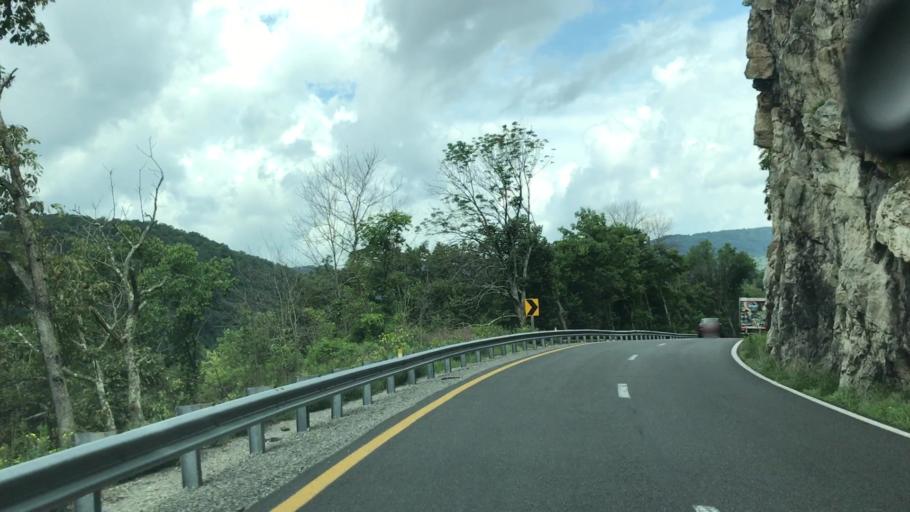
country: US
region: Virginia
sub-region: Giles County
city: Narrows
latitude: 37.3681
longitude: -80.8184
